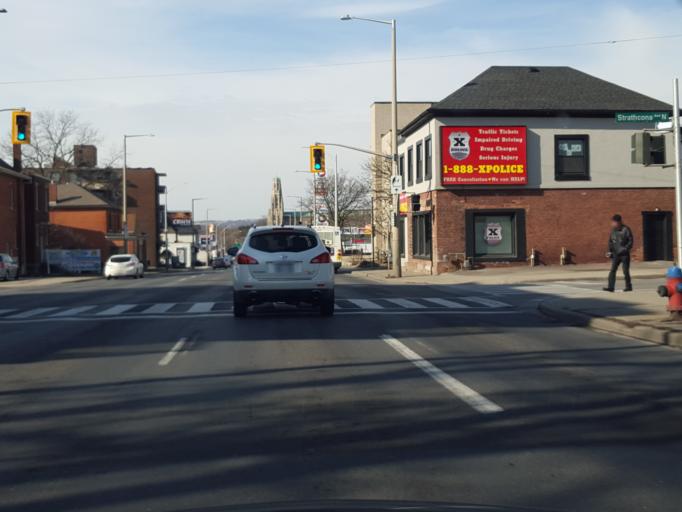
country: CA
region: Ontario
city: Hamilton
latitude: 43.2613
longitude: -79.8850
